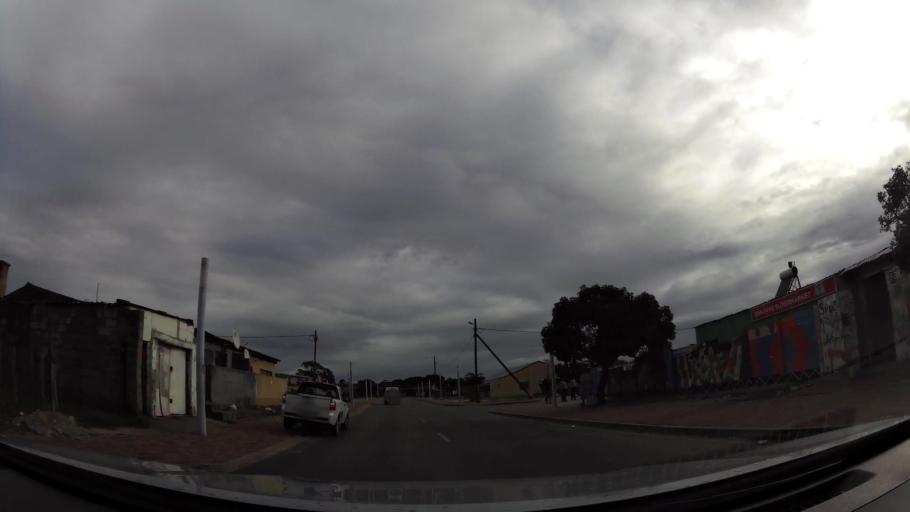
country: ZA
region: Eastern Cape
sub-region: Nelson Mandela Bay Metropolitan Municipality
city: Port Elizabeth
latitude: -33.9867
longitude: 25.5887
